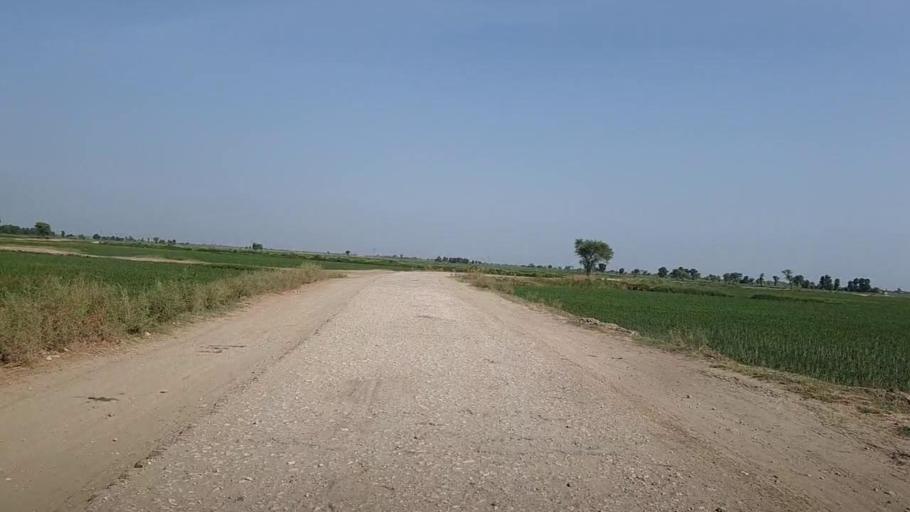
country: PK
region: Sindh
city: Mehar
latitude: 27.1123
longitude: 67.8463
